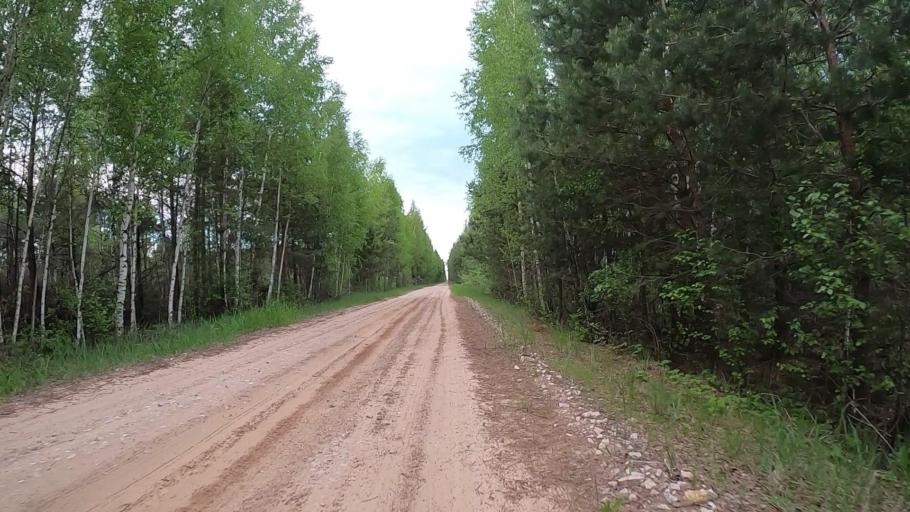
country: LV
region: Olaine
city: Olaine
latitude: 56.8445
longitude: 23.9353
